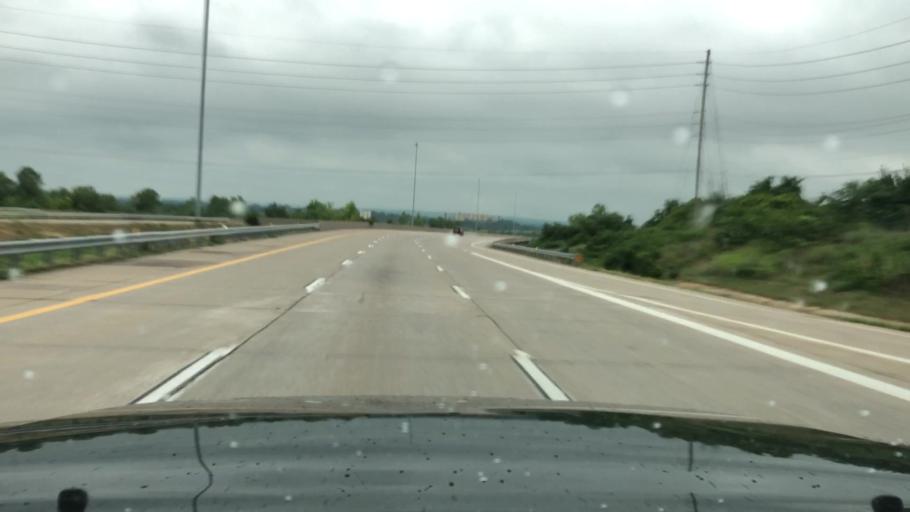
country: US
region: Missouri
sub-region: Saint Charles County
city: Saint Peters
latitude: 38.8018
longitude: -90.5898
